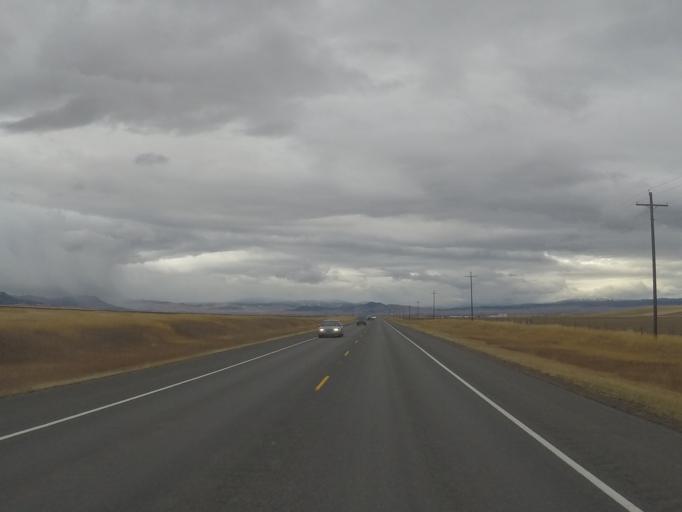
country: US
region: Montana
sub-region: Lewis and Clark County
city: East Helena
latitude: 46.5785
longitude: -111.8415
